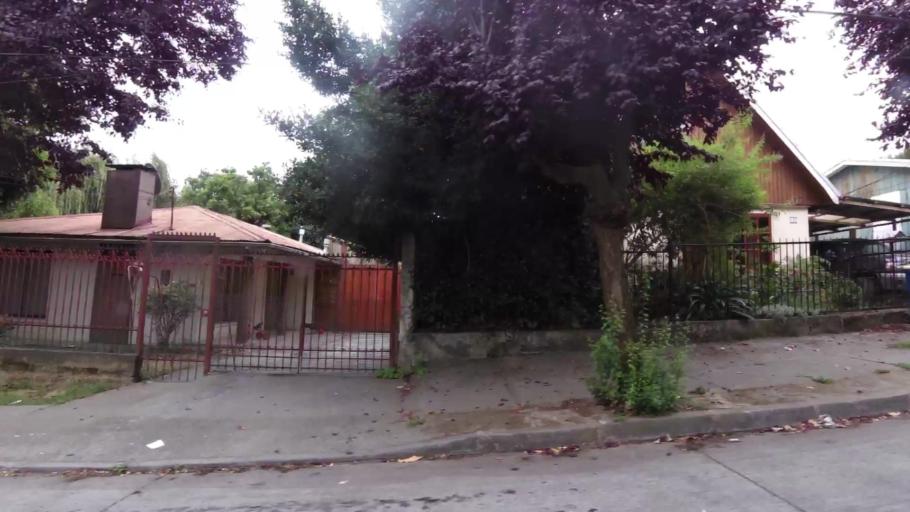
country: CL
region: Biobio
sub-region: Provincia de Concepcion
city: Concepcion
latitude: -36.8237
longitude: -73.0071
